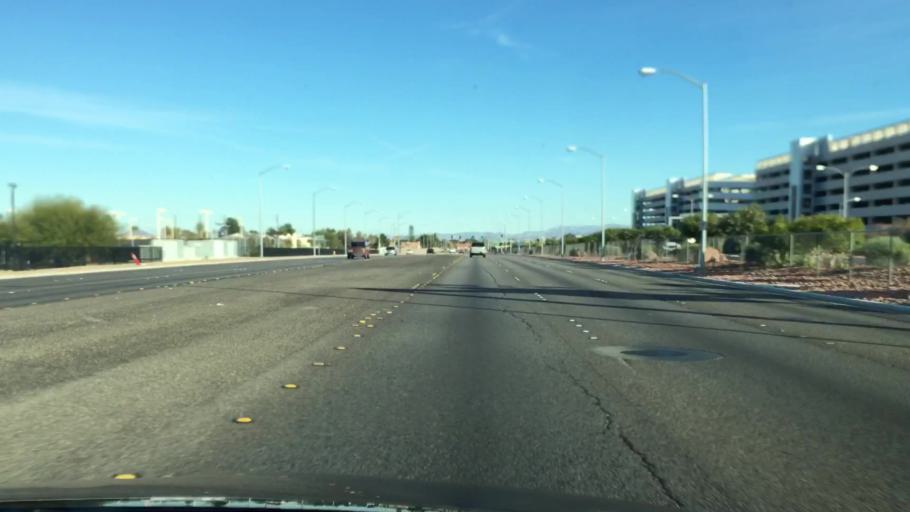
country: US
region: Nevada
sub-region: Clark County
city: Paradise
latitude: 36.0889
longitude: -115.1403
